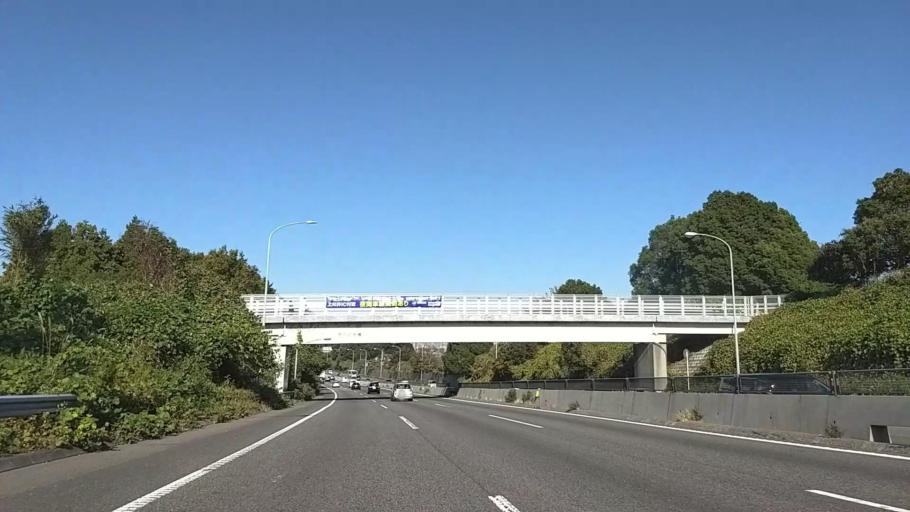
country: JP
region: Kanagawa
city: Minami-rinkan
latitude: 35.4740
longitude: 139.5297
